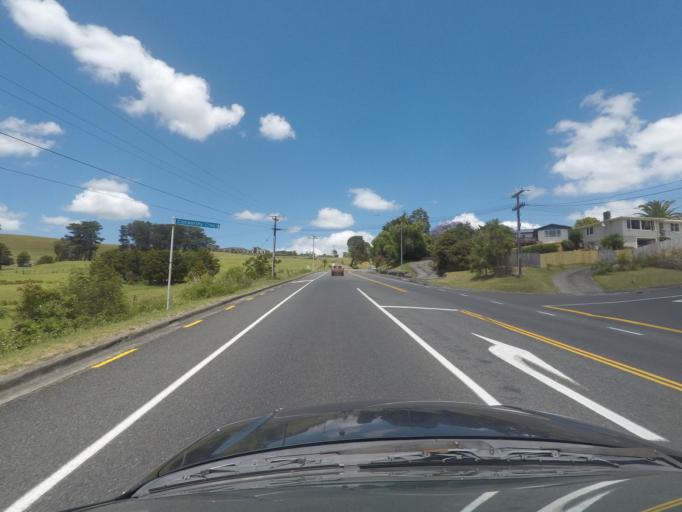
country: NZ
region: Northland
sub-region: Whangarei
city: Whangarei
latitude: -35.7417
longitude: 174.3644
